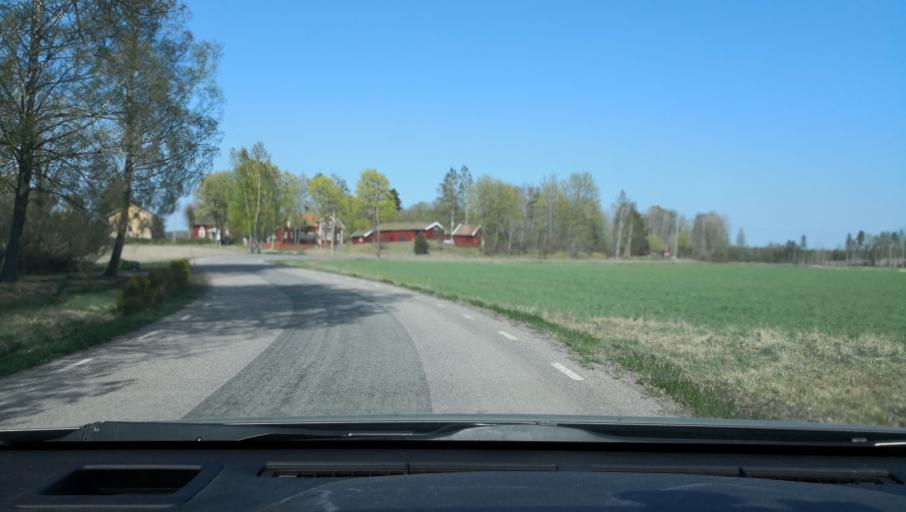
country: SE
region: Uppsala
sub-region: Heby Kommun
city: Heby
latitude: 60.0345
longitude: 16.8021
